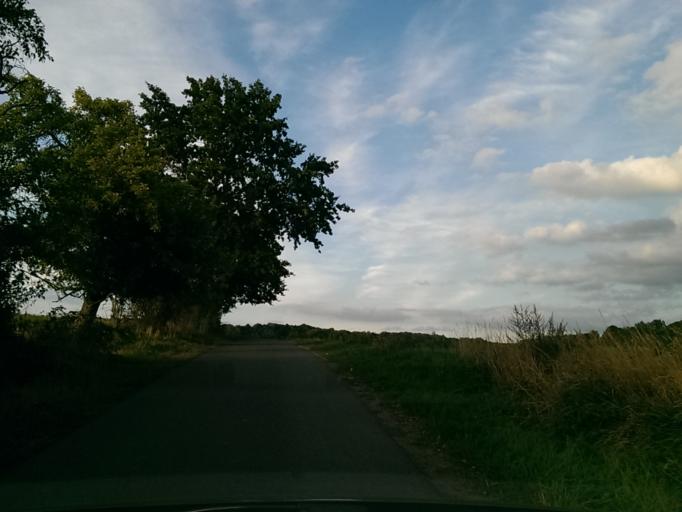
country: CZ
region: Central Bohemia
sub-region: Okres Mlada Boleslav
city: Zd'ar
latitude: 50.5403
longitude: 15.1220
